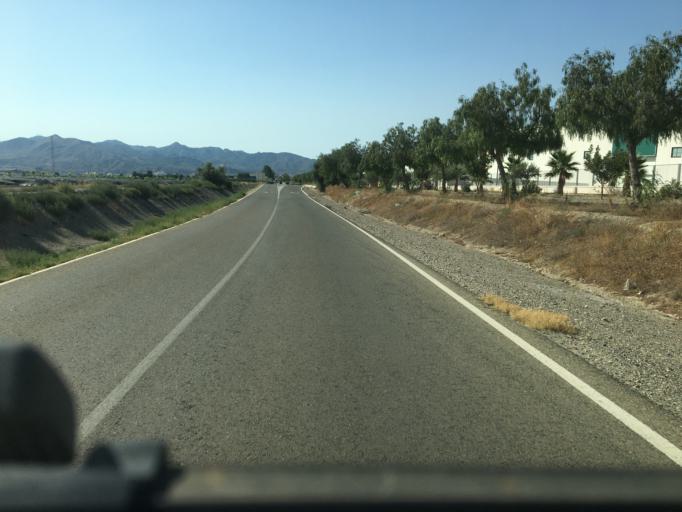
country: ES
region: Andalusia
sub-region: Provincia de Almeria
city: Huercal-Overa
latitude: 37.4185
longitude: -1.9683
